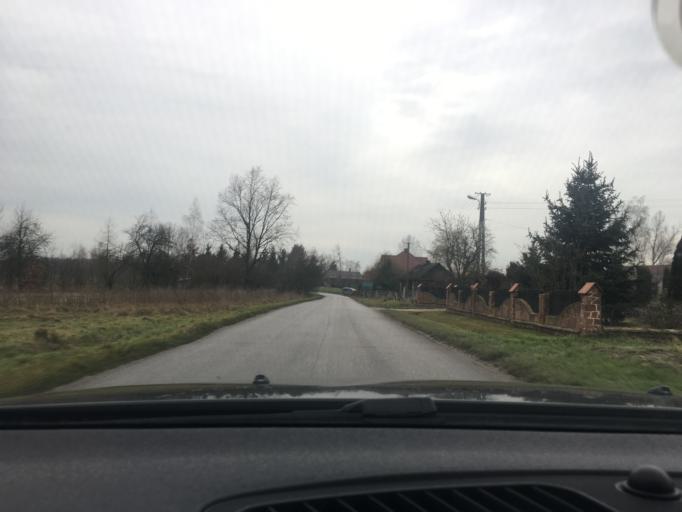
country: PL
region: Swietokrzyskie
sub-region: Powiat jedrzejowski
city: Imielno
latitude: 50.6415
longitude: 20.4079
